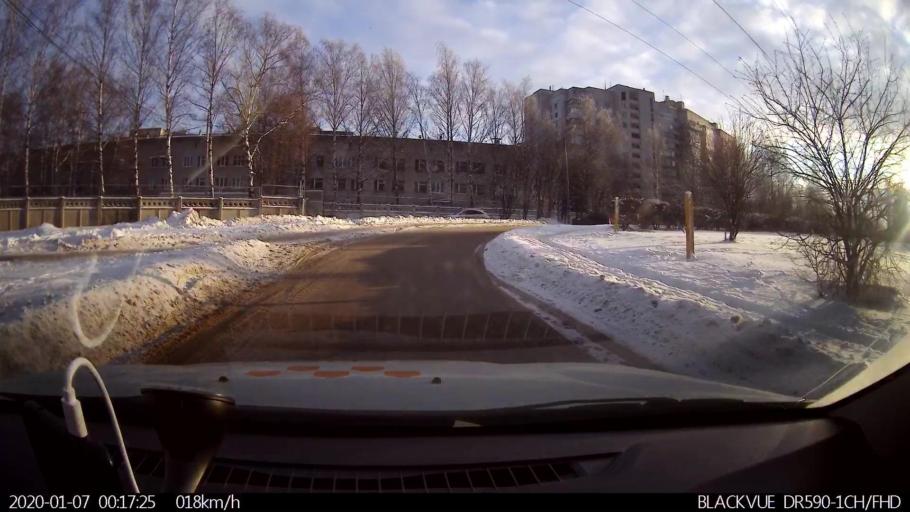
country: RU
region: Nizjnij Novgorod
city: Nizhniy Novgorod
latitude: 56.2339
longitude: 43.9434
